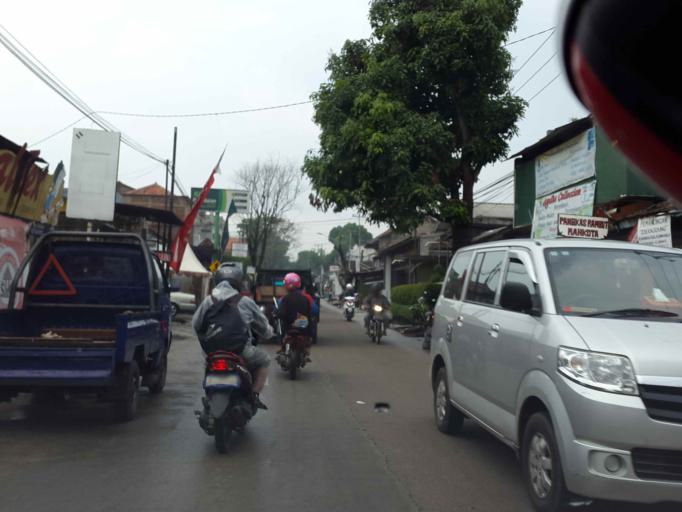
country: ID
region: West Java
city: Cimahi
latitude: -6.8719
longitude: 107.5568
